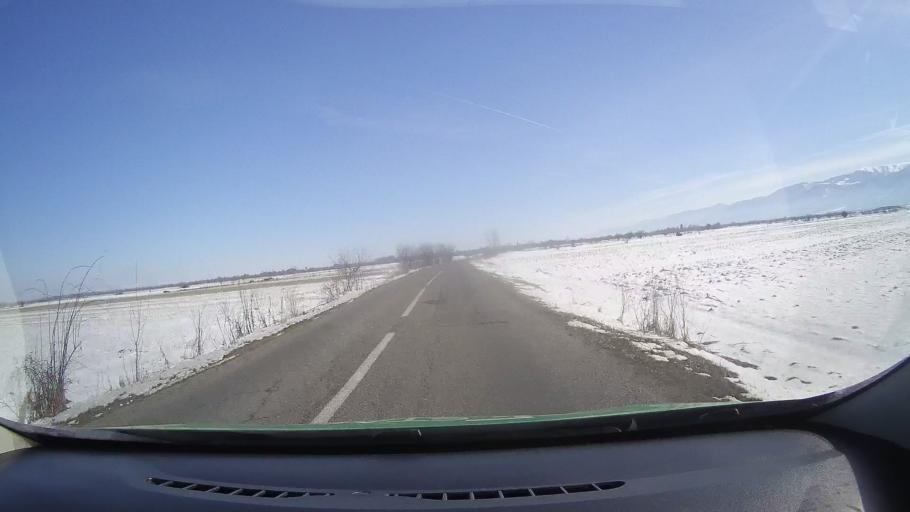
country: RO
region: Brasov
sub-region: Comuna Lisa
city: Lisa
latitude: 45.7277
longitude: 24.8848
